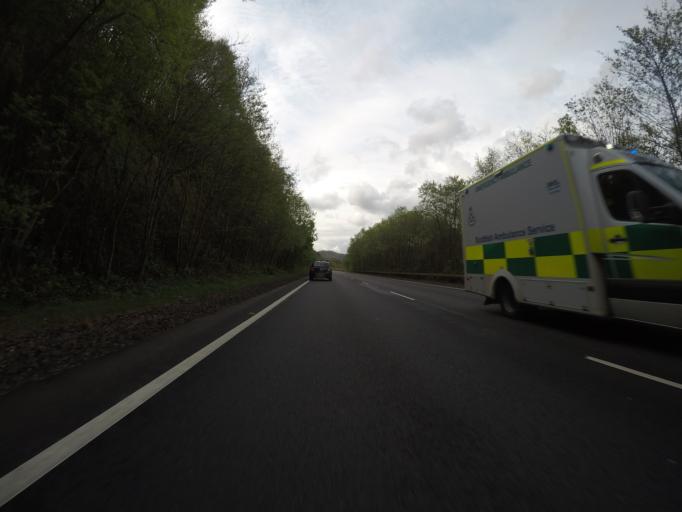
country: GB
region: Scotland
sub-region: Argyll and Bute
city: Helensburgh
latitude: 56.1383
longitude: -4.6602
